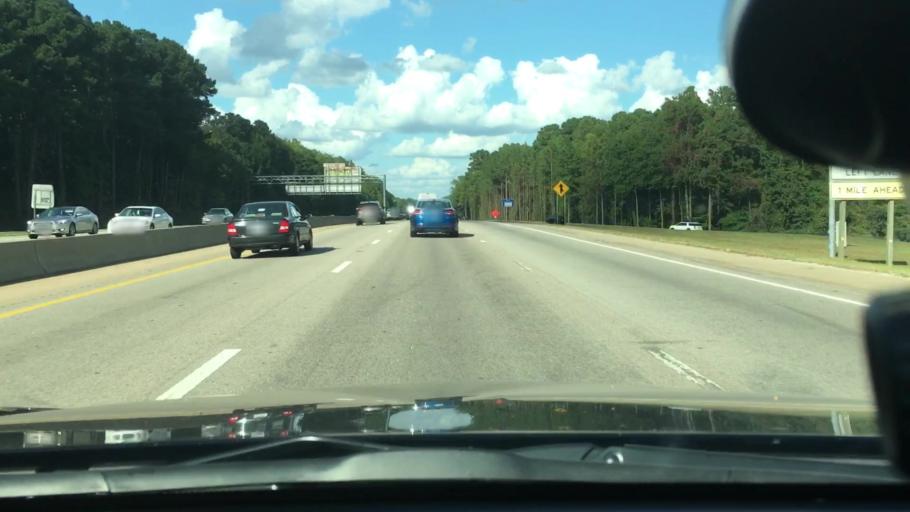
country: US
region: North Carolina
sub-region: Wake County
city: West Raleigh
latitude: 35.8166
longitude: -78.6899
